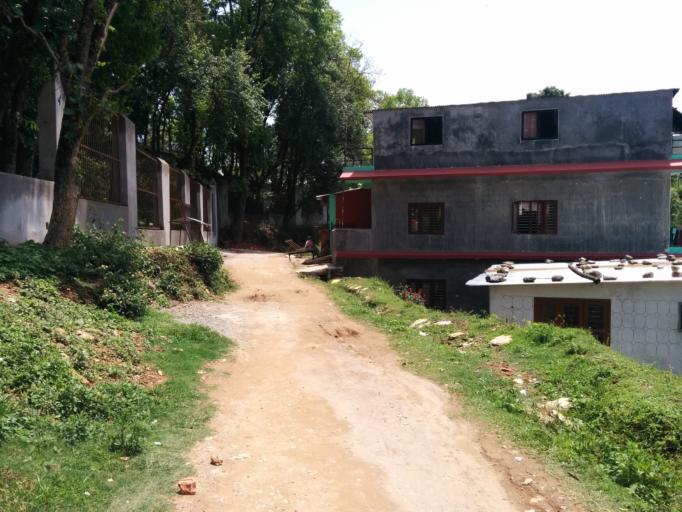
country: NP
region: Western Region
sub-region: Gandaki Zone
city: Pokhara
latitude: 28.1946
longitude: 83.9665
